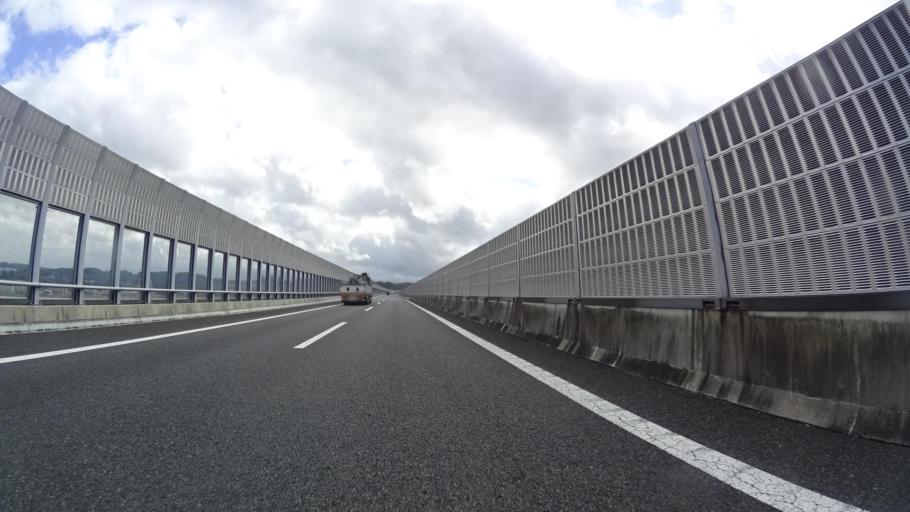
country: JP
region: Shiga Prefecture
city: Minakuchicho-matoba
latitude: 34.9112
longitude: 136.1810
